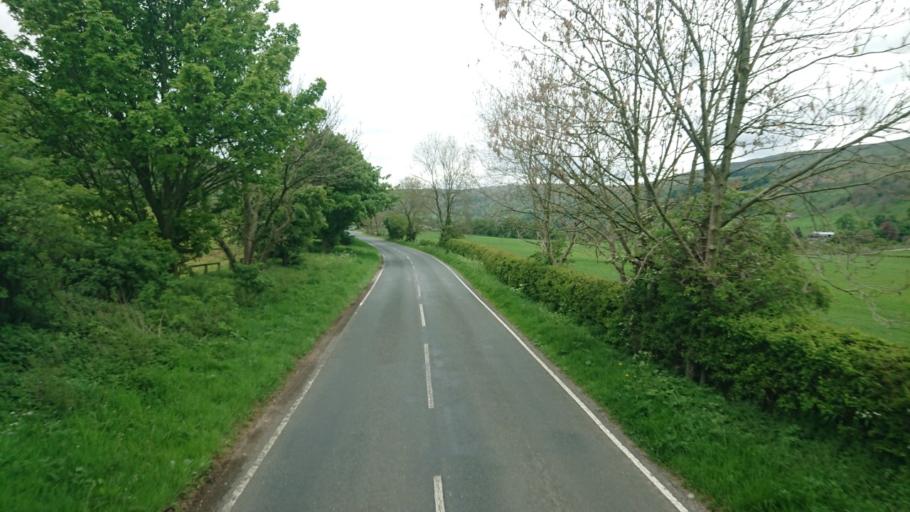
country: GB
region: England
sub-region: North Yorkshire
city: Leyburn
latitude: 54.2588
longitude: -2.0276
